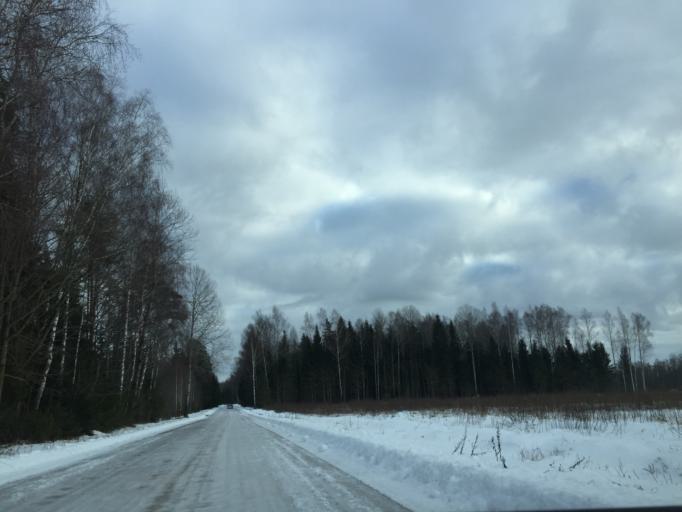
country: LV
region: Lielvarde
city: Lielvarde
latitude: 56.5837
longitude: 24.7415
